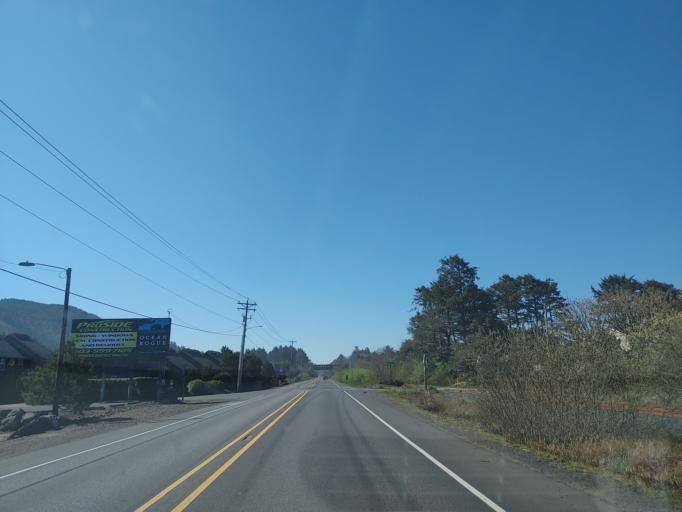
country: US
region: Oregon
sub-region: Tillamook County
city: Rockaway Beach
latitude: 45.5964
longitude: -123.9467
